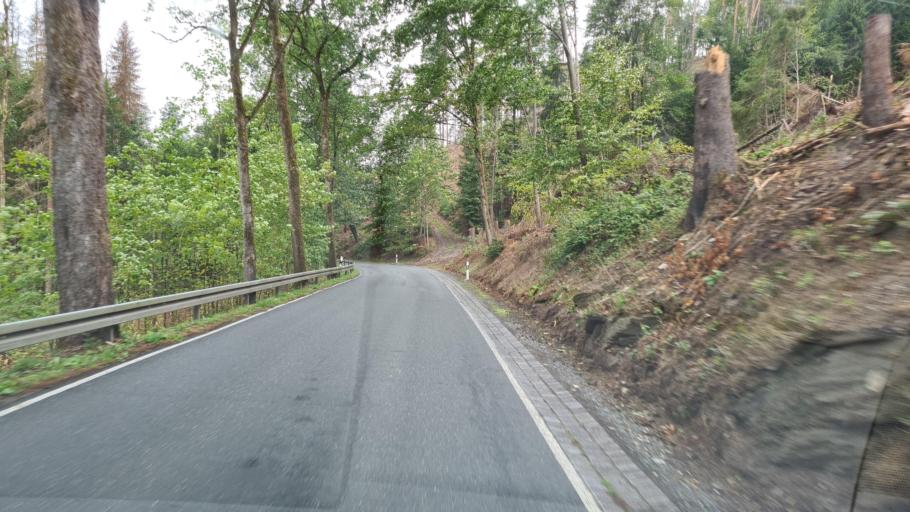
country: DE
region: Thuringia
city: Leutenberg
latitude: 50.5315
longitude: 11.4987
